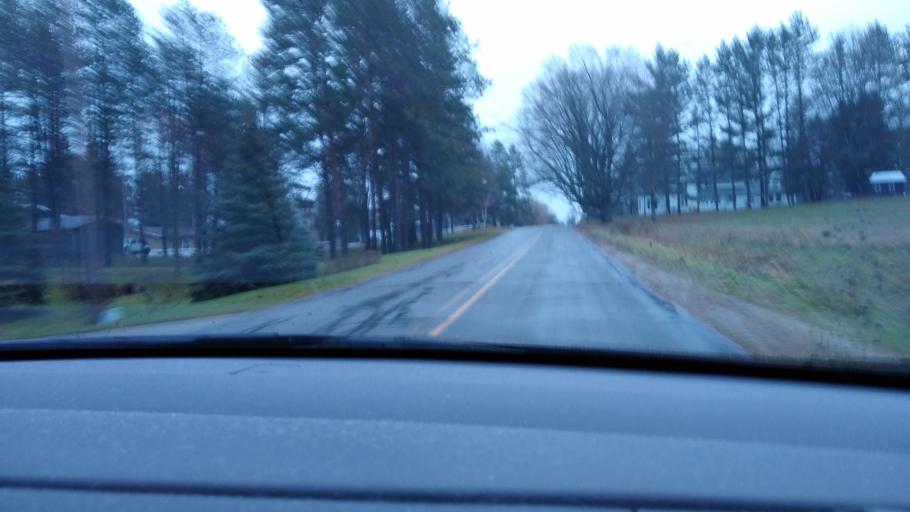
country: US
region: Michigan
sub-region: Wexford County
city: Cadillac
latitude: 44.1813
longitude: -85.3954
